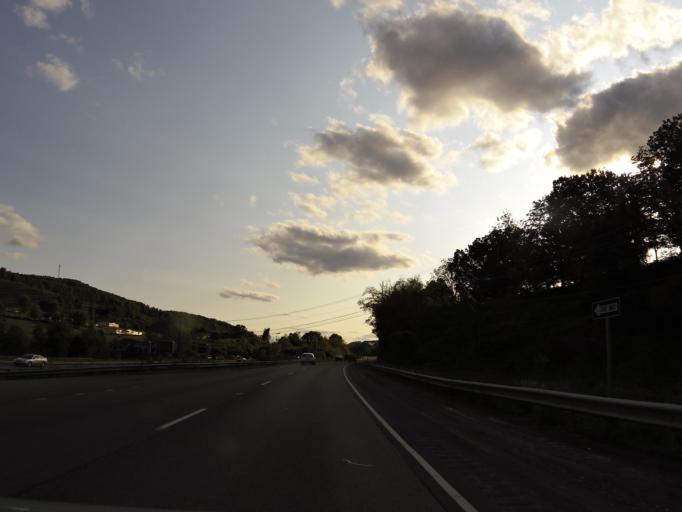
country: US
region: Virginia
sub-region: Russell County
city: Honaker
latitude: 36.9583
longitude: -81.9337
